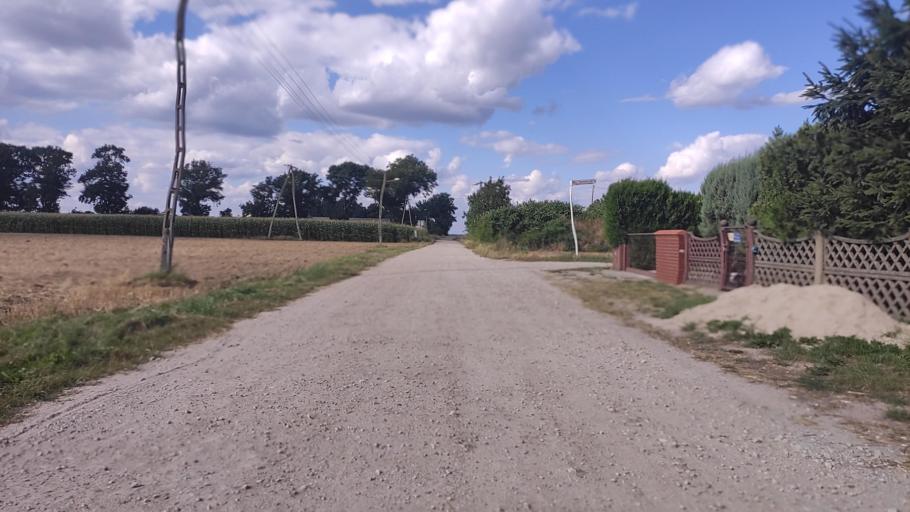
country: PL
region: Greater Poland Voivodeship
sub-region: Powiat poznanski
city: Swarzedz
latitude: 52.4120
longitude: 17.1399
